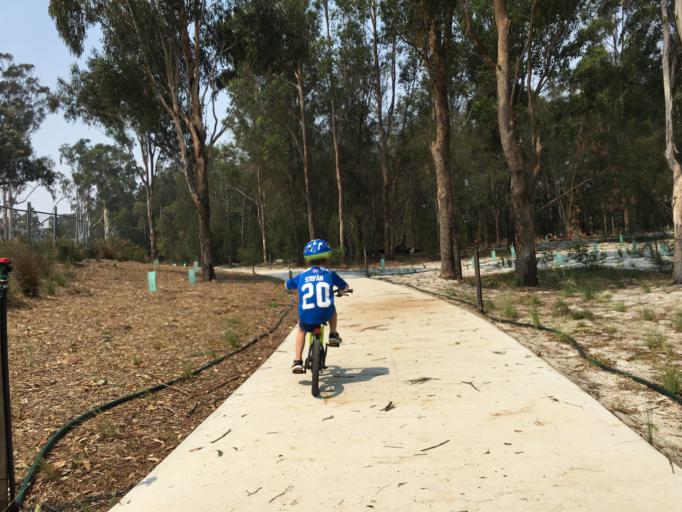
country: AU
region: New South Wales
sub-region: Campbelltown Municipality
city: Denham Court
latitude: -33.9743
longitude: 150.8158
